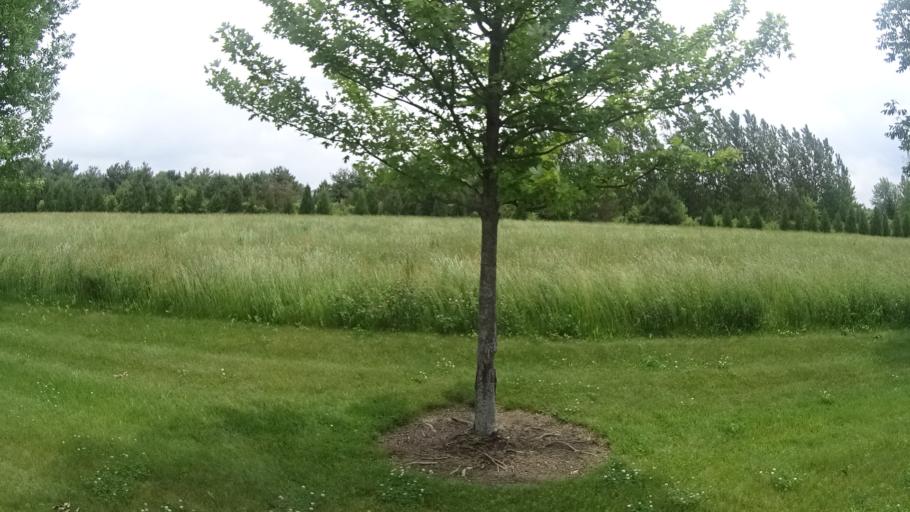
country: US
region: Ohio
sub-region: Huron County
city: Bellevue
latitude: 41.3245
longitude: -82.8230
